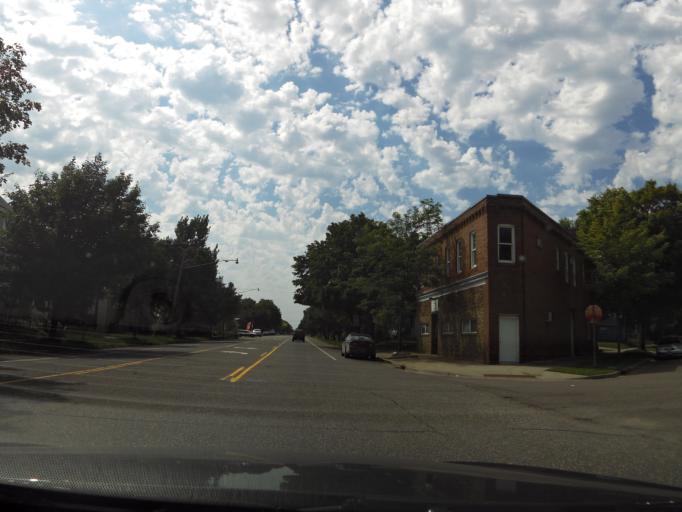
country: US
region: Minnesota
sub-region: Dakota County
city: West Saint Paul
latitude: 44.9233
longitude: -93.1333
